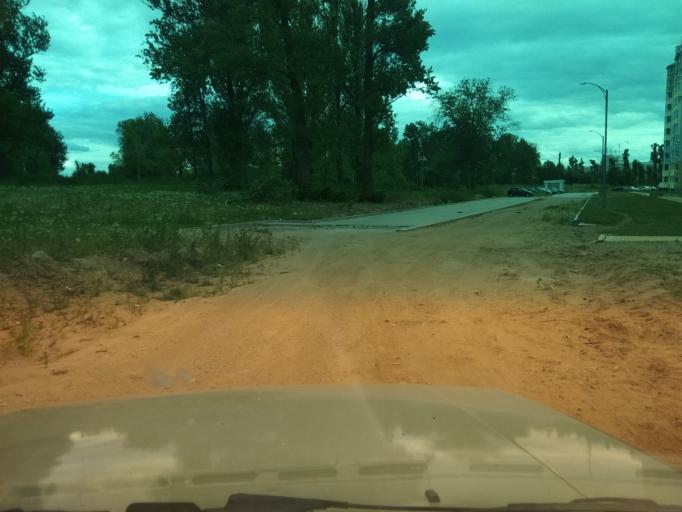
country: BY
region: Mogilev
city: Mahilyow
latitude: 53.9235
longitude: 30.3548
